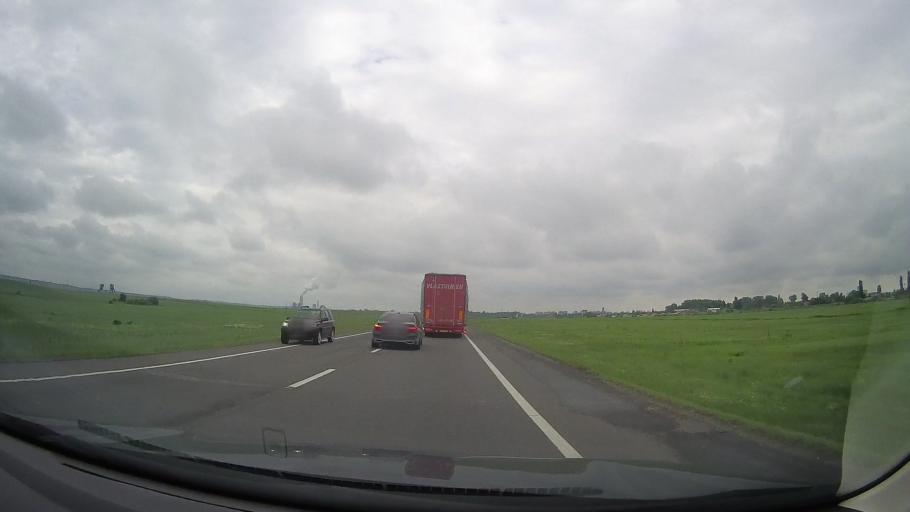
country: RO
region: Dolj
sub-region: Municipiul Craiova
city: Cernele
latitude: 44.3626
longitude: 23.7593
